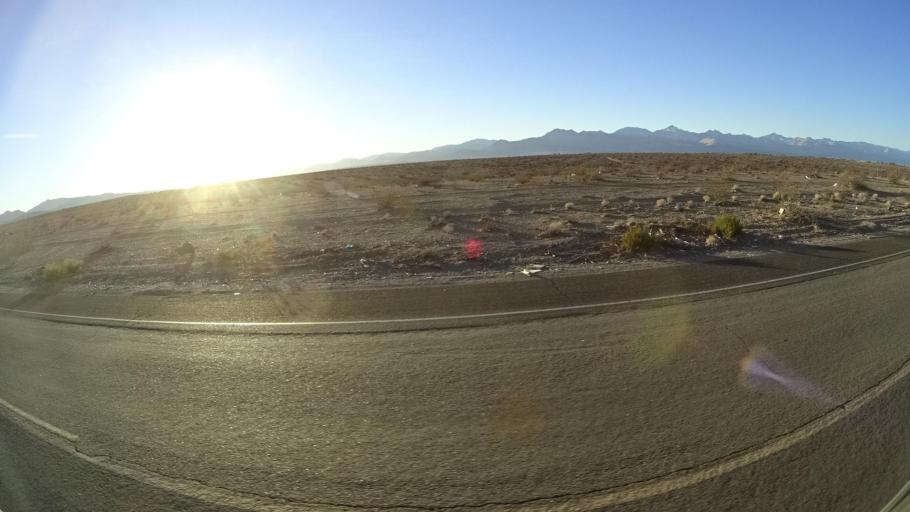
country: US
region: California
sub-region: Kern County
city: China Lake Acres
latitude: 35.6147
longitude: -117.7230
